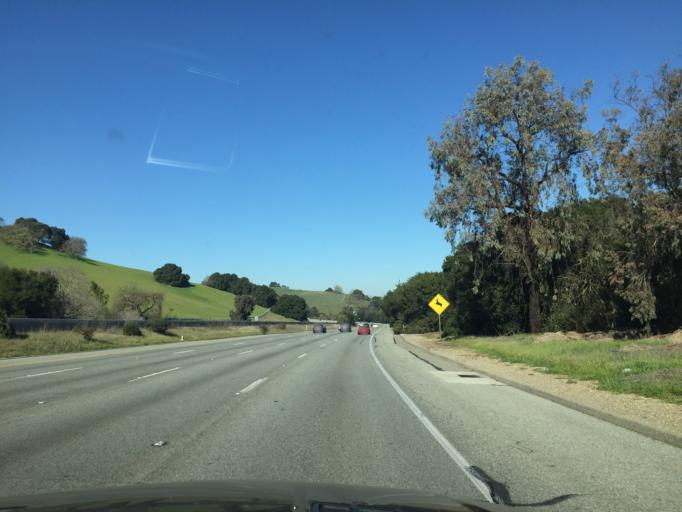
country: US
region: California
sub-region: Santa Clara County
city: Los Altos Hills
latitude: 37.3807
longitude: -122.1511
